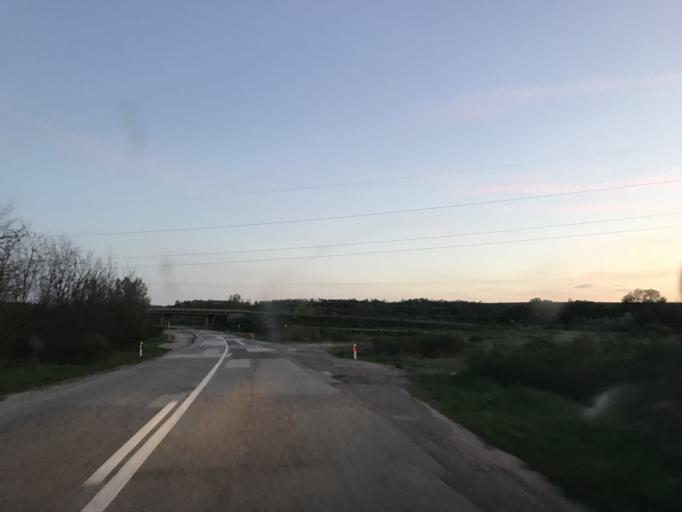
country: RS
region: Central Serbia
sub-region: Zajecarski Okrug
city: Zajecar
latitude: 43.9802
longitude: 22.2925
